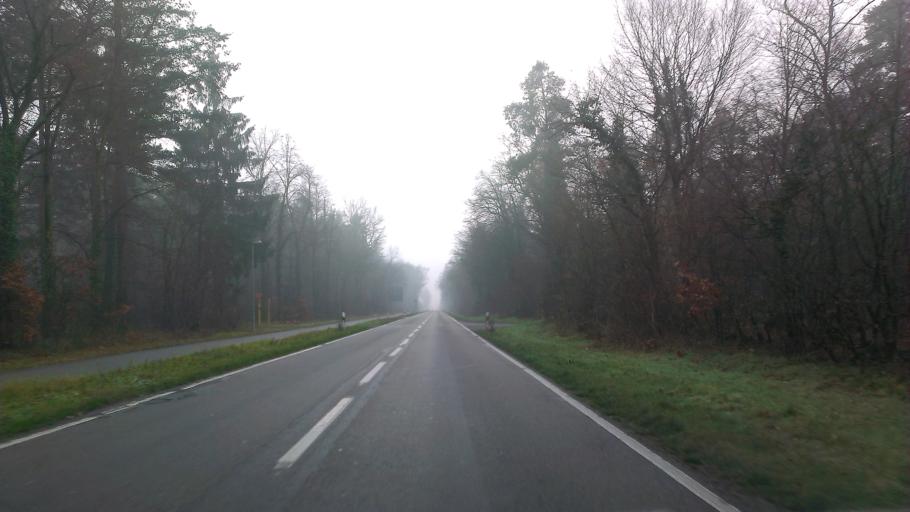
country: DE
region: Baden-Wuerttemberg
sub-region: Karlsruhe Region
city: Waghausel
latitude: 49.2325
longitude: 8.5331
